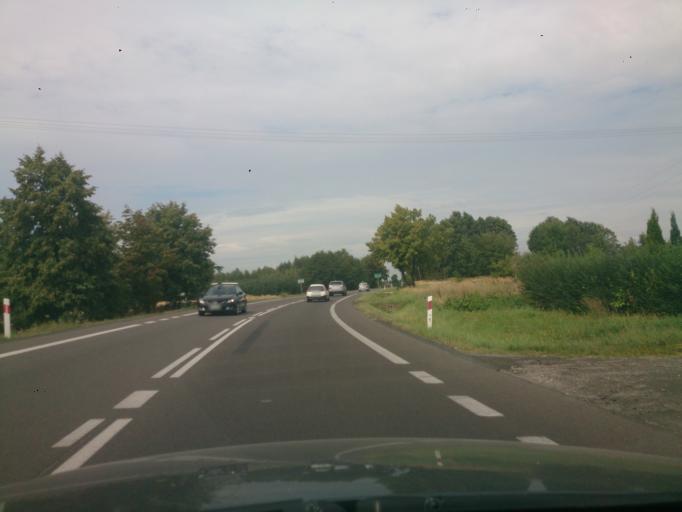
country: PL
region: Subcarpathian Voivodeship
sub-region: Powiat kolbuszowski
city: Dzikowiec
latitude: 50.2030
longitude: 21.8347
